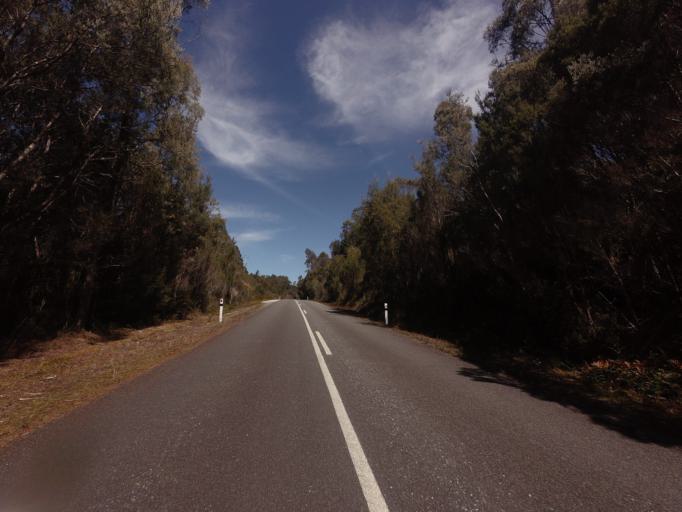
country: AU
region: Tasmania
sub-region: West Coast
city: Queenstown
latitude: -42.7698
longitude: 146.0437
